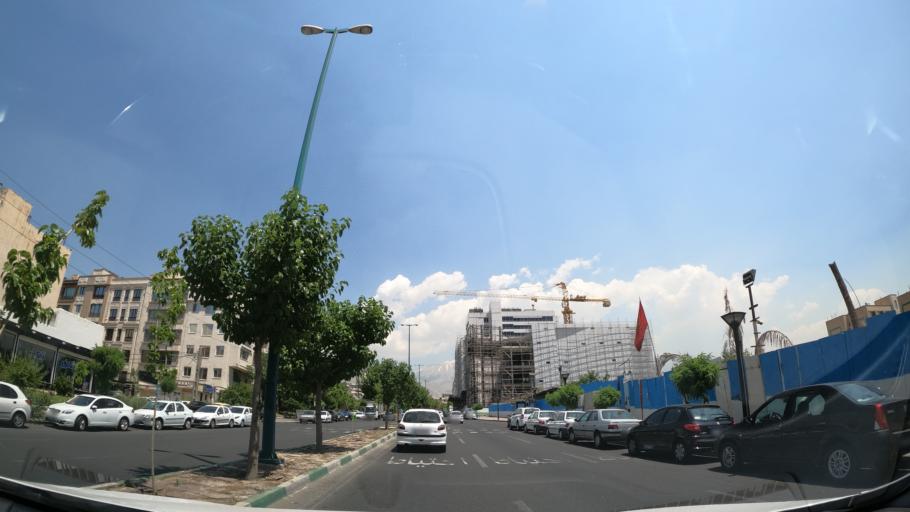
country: IR
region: Tehran
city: Tajrish
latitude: 35.7687
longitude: 51.3788
